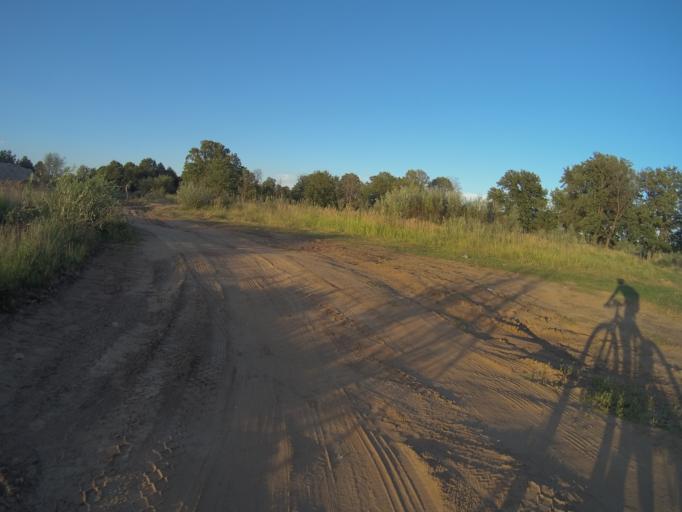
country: RU
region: Vladimir
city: Kommunar
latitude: 56.0859
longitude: 40.4197
